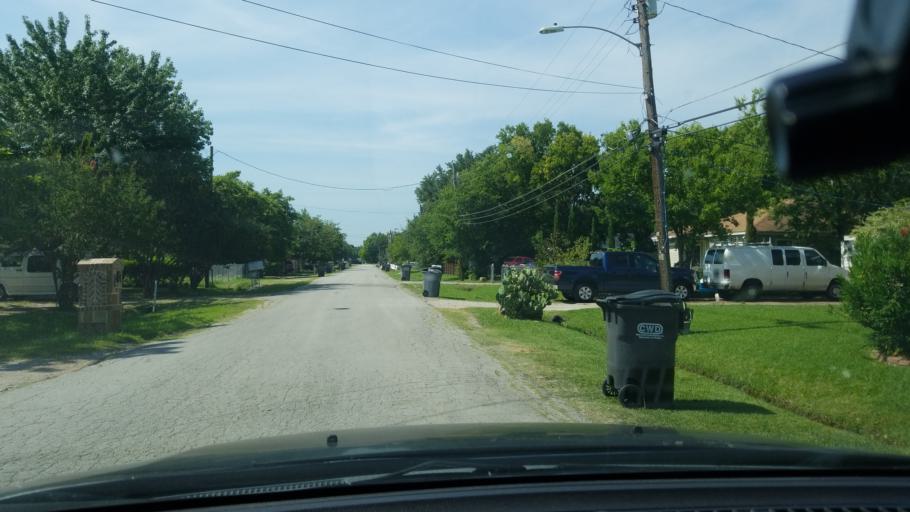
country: US
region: Texas
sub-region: Dallas County
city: Balch Springs
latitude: 32.7366
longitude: -96.6265
